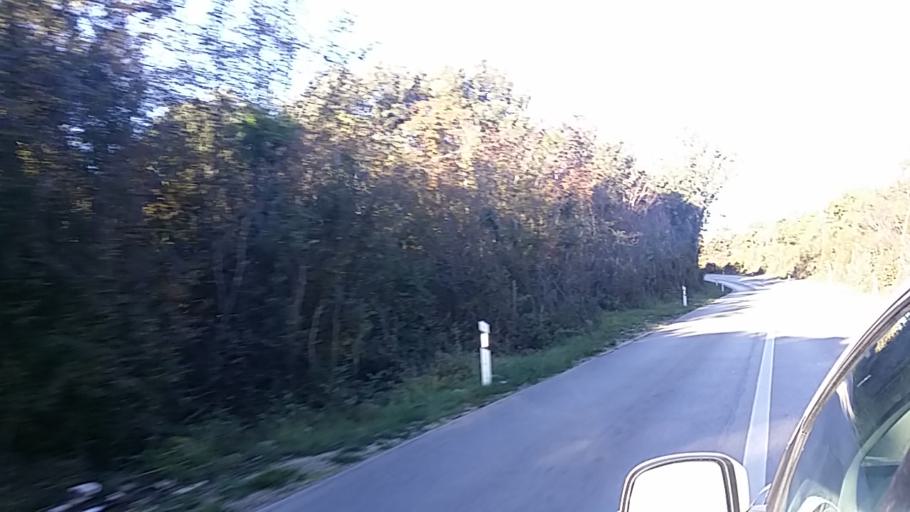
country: HR
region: Istarska
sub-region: Grad Rovinj
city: Rovinj
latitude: 45.1407
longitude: 13.7167
